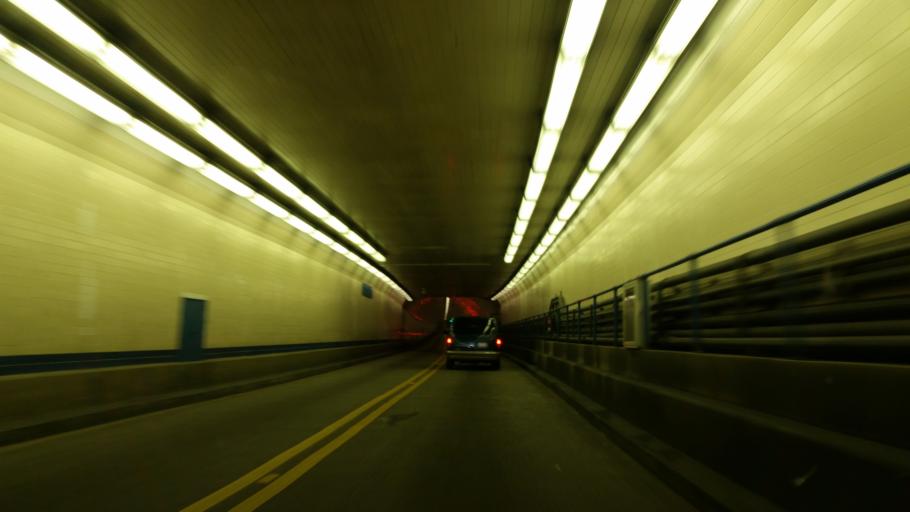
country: US
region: Alabama
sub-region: Mobile County
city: Mobile
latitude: 30.6904
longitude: -88.0401
